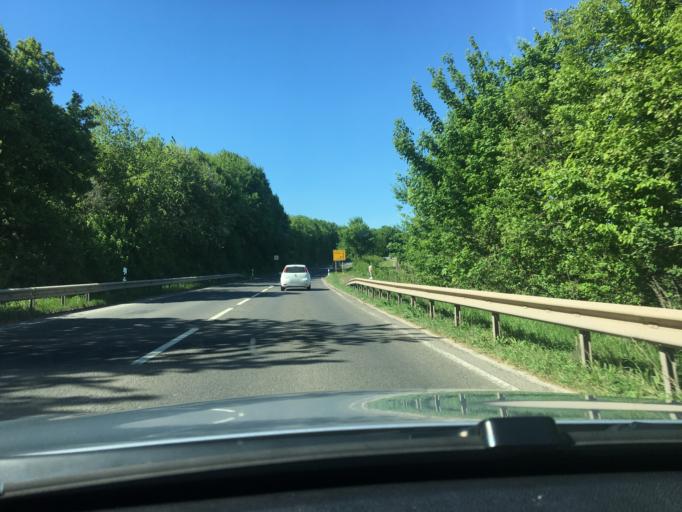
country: DE
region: Rheinland-Pfalz
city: Hackenheim
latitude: 49.8277
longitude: 7.9056
